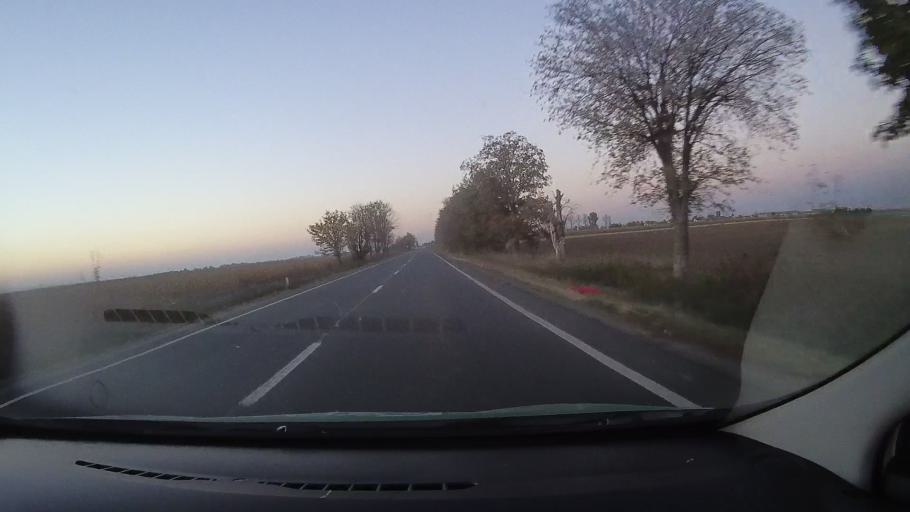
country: RO
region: Bihor
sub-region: Comuna Tarcea
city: Tarcea
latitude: 47.4759
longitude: 22.1640
